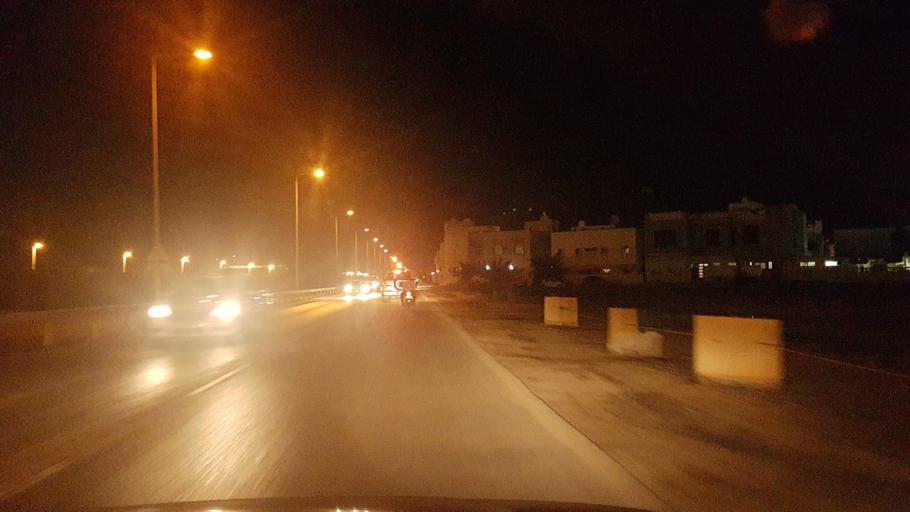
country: BH
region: Muharraq
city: Al Muharraq
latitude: 26.2782
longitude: 50.6331
